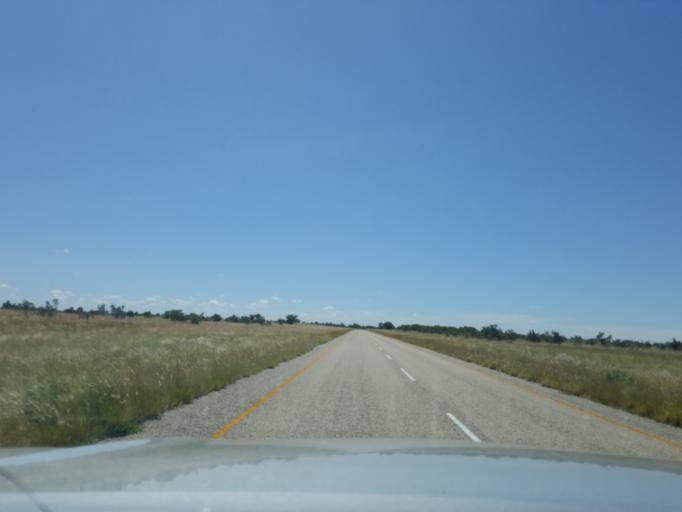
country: BW
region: Central
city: Gweta
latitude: -20.2142
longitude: 25.0839
